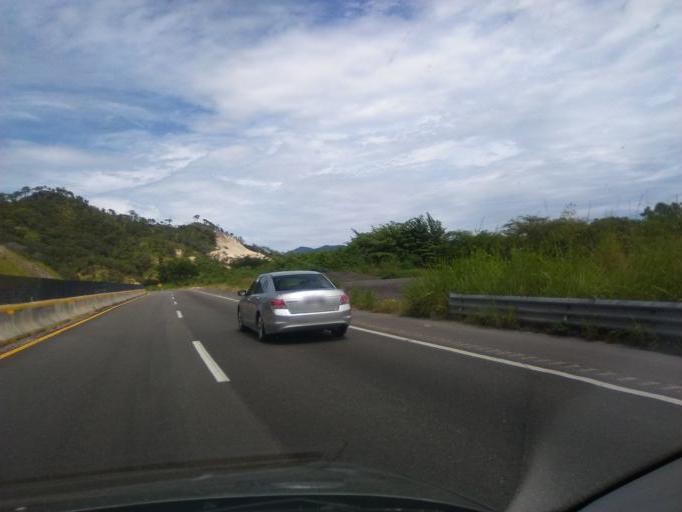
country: MX
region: Guerrero
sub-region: Chilpancingo de los Bravo
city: Cajelitos
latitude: 17.3155
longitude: -99.4859
